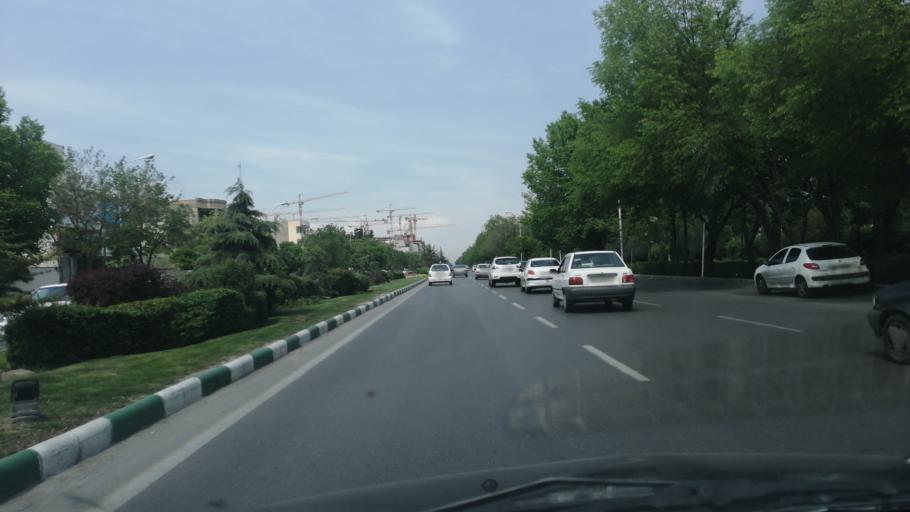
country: IR
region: Razavi Khorasan
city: Mashhad
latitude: 36.3106
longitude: 59.5558
